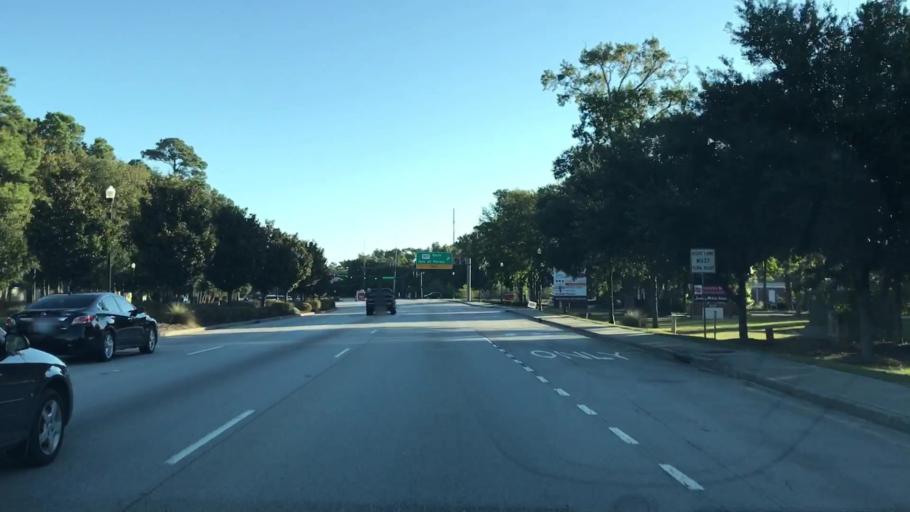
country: US
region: South Carolina
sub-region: Charleston County
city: Mount Pleasant
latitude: 32.8325
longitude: -79.8277
